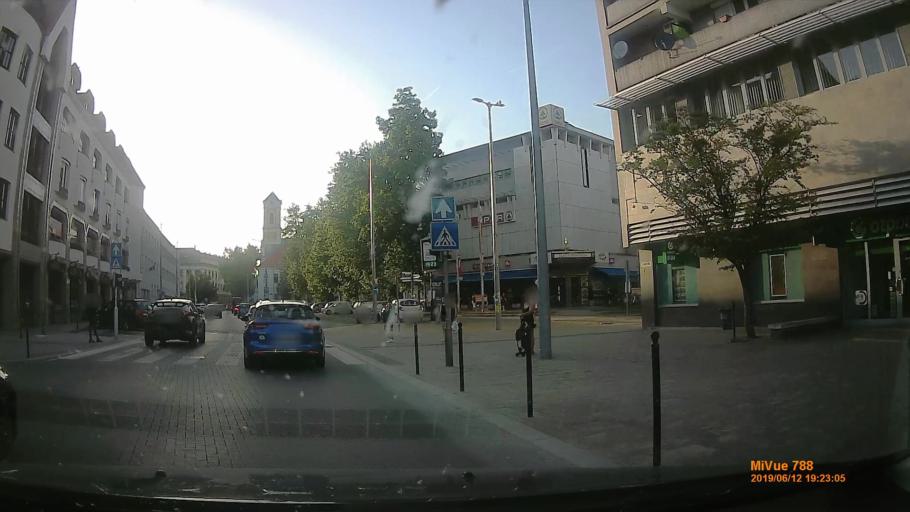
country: HU
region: Bacs-Kiskun
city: Kecskemet
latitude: 46.9091
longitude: 19.6938
